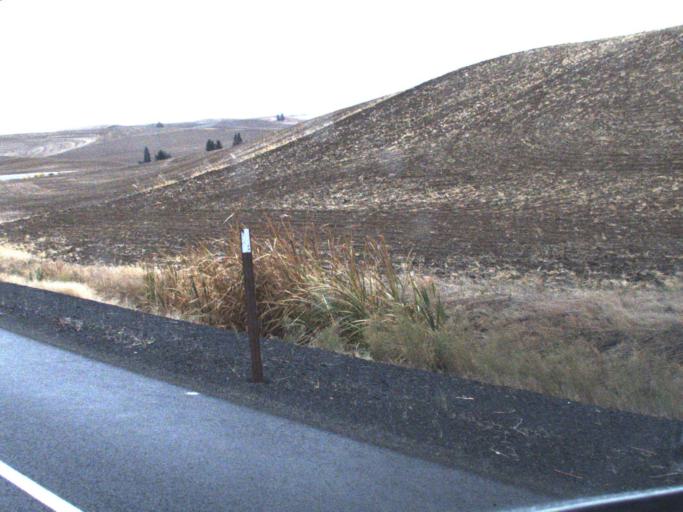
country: US
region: Washington
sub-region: Whitman County
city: Pullman
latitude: 46.7594
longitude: -117.2442
